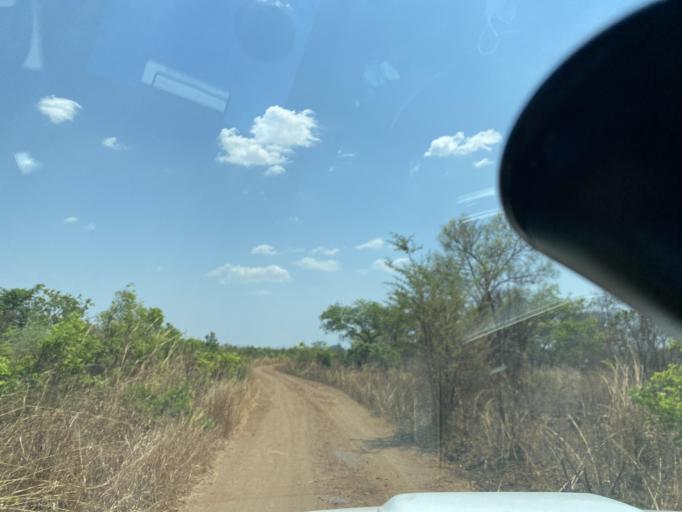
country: ZM
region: Lusaka
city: Lusaka
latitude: -15.5078
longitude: 27.9858
